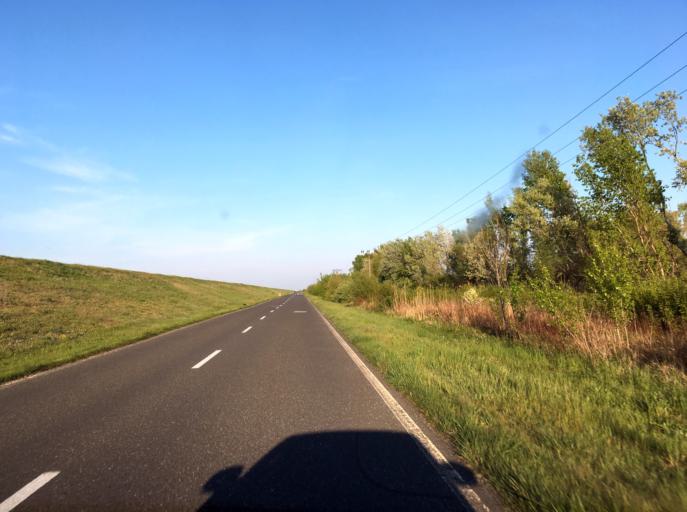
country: SK
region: Trnavsky
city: Samorin
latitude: 47.9966
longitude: 17.2837
